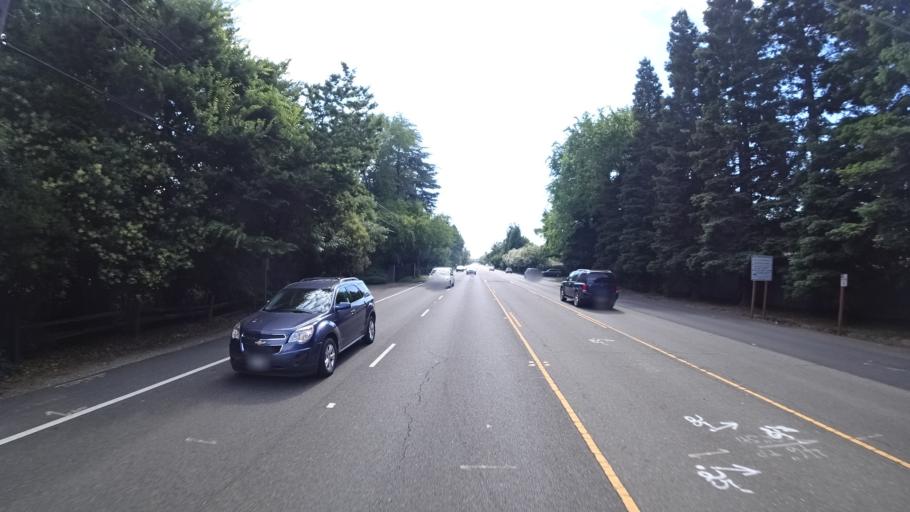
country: US
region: California
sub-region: Sacramento County
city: Arden-Arcade
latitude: 38.5742
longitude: -121.3974
